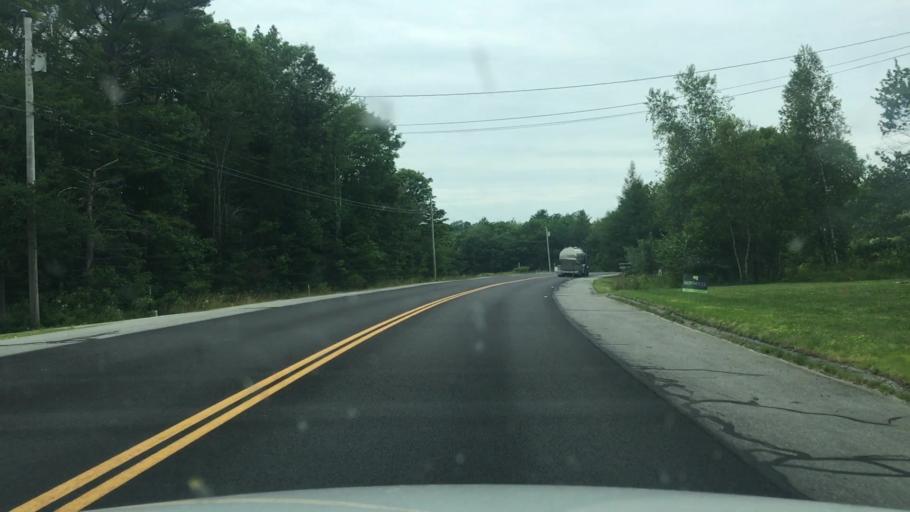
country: US
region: Maine
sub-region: Knox County
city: Washington
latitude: 44.3683
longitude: -69.3860
